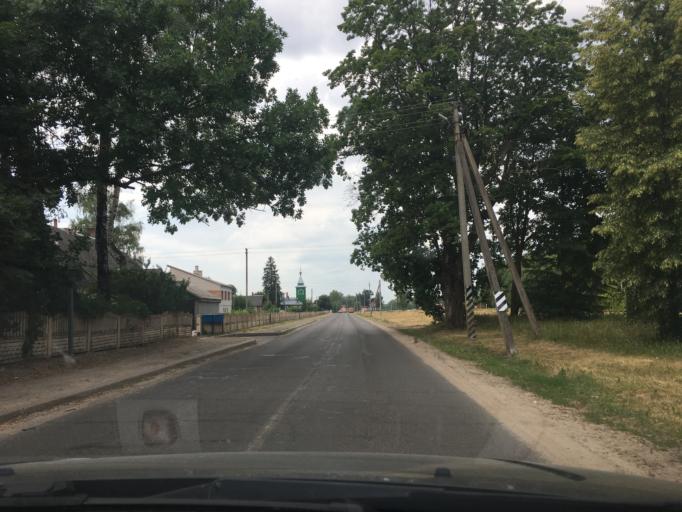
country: LT
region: Alytaus apskritis
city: Druskininkai
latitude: 53.8910
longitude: 24.1406
